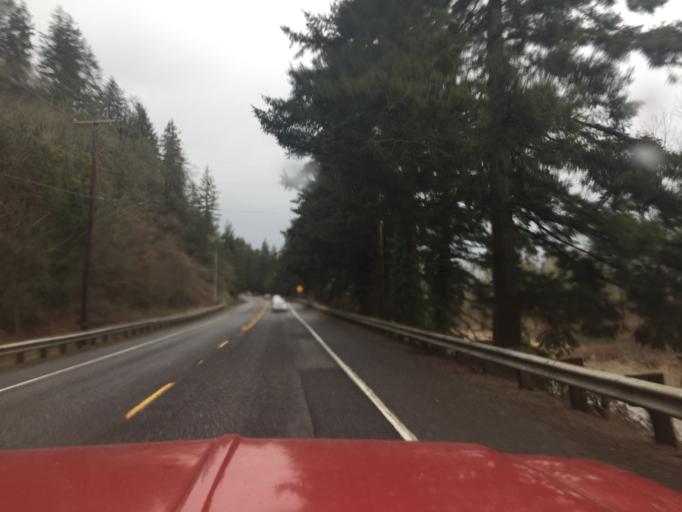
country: US
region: Oregon
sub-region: Columbia County
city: Rainier
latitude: 46.0565
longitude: -122.8960
